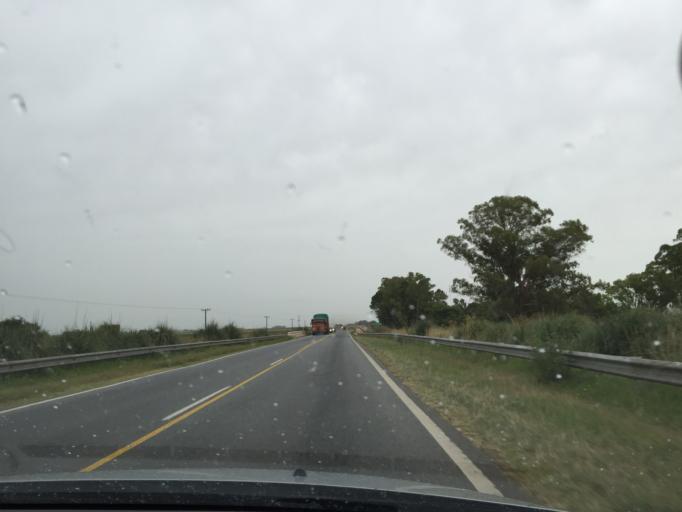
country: AR
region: Buenos Aires
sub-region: Partido de Tandil
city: Tandil
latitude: -37.5582
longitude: -58.7929
